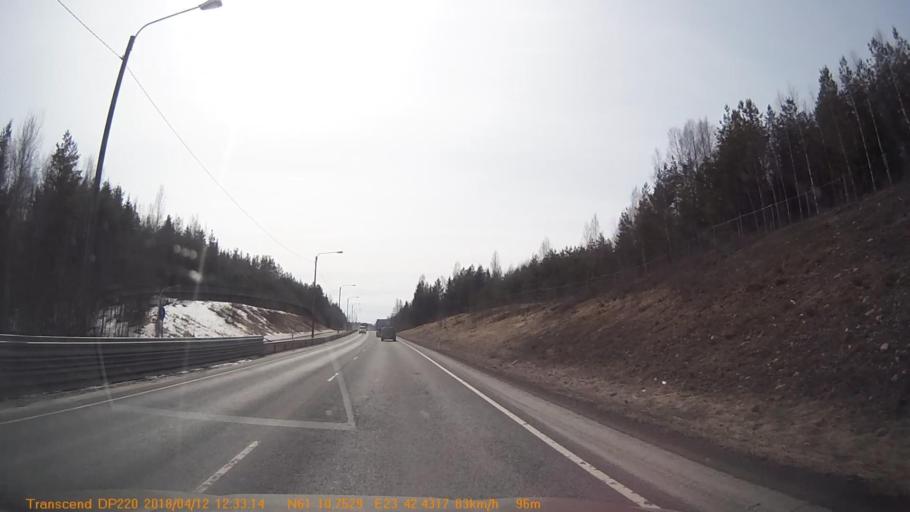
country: FI
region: Pirkanmaa
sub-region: Etelae-Pirkanmaa
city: Kylmaekoski
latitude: 61.1790
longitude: 23.7071
